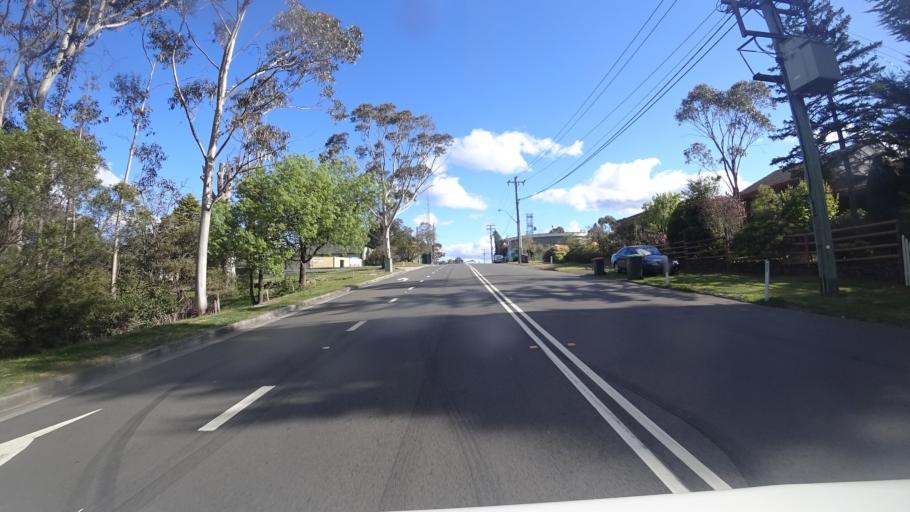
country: AU
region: New South Wales
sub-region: Blue Mountains Municipality
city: Katoomba
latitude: -33.7089
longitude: 150.3005
